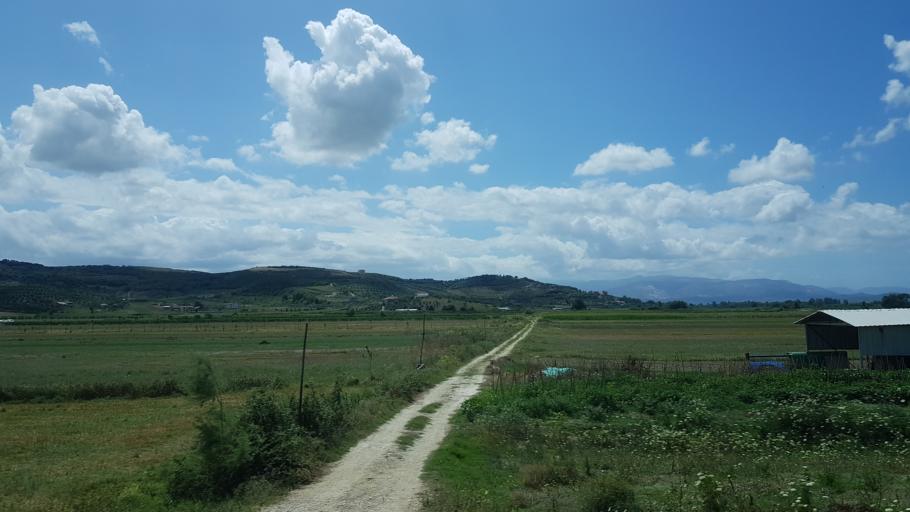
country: AL
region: Fier
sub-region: Rrethi i Fierit
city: Cakran
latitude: 40.5943
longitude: 19.5816
